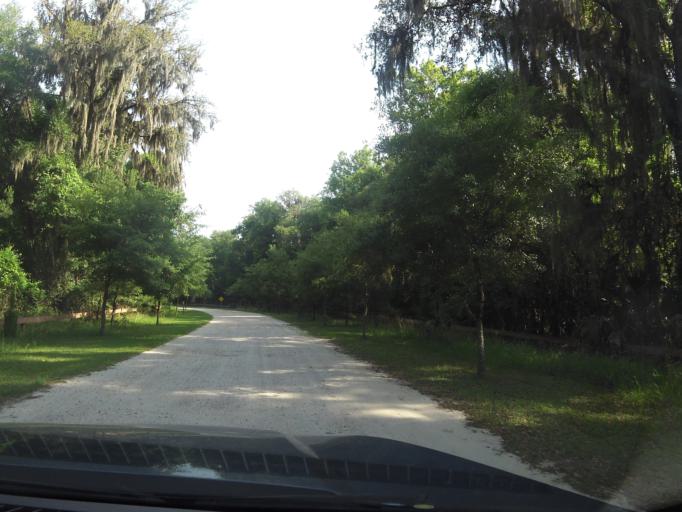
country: US
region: Florida
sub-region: Duval County
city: Atlantic Beach
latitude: 30.4842
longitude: -81.4903
